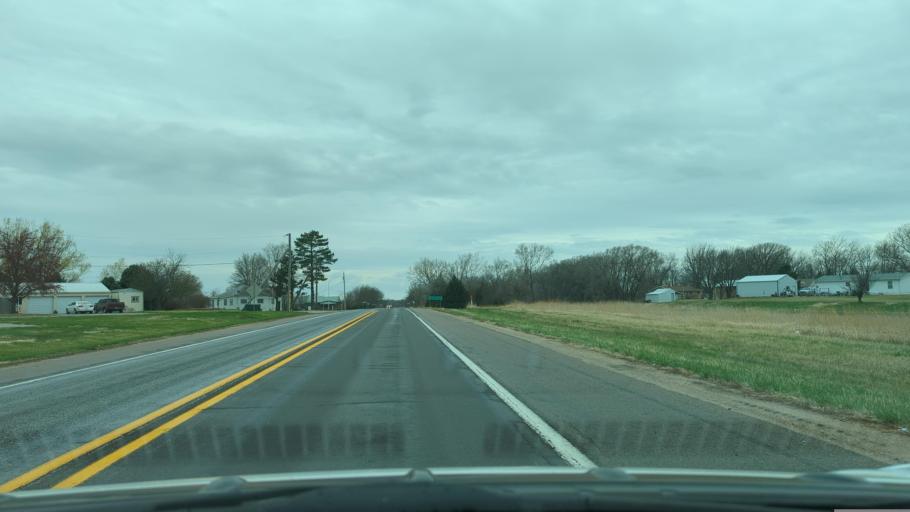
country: US
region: Nebraska
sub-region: Lancaster County
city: Waverly
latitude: 40.9598
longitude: -96.4441
